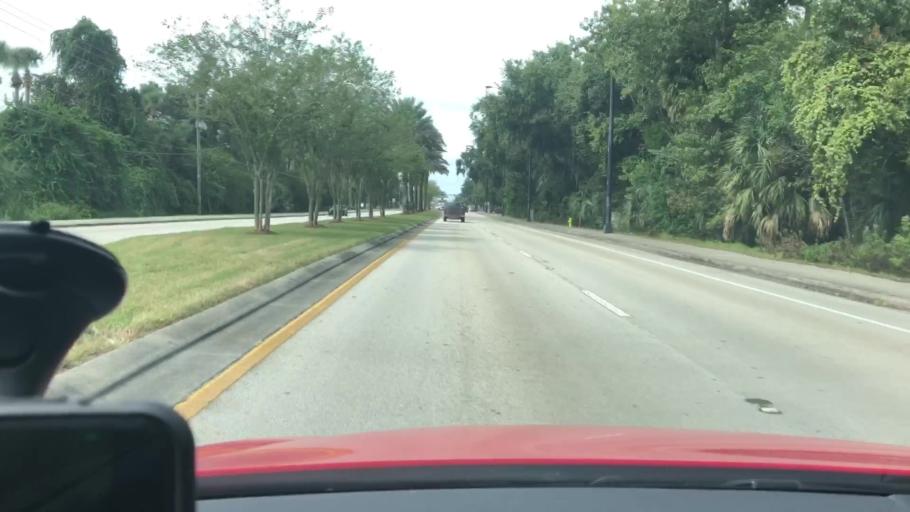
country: US
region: Florida
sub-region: Volusia County
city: Port Orange
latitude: 29.1215
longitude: -81.0017
